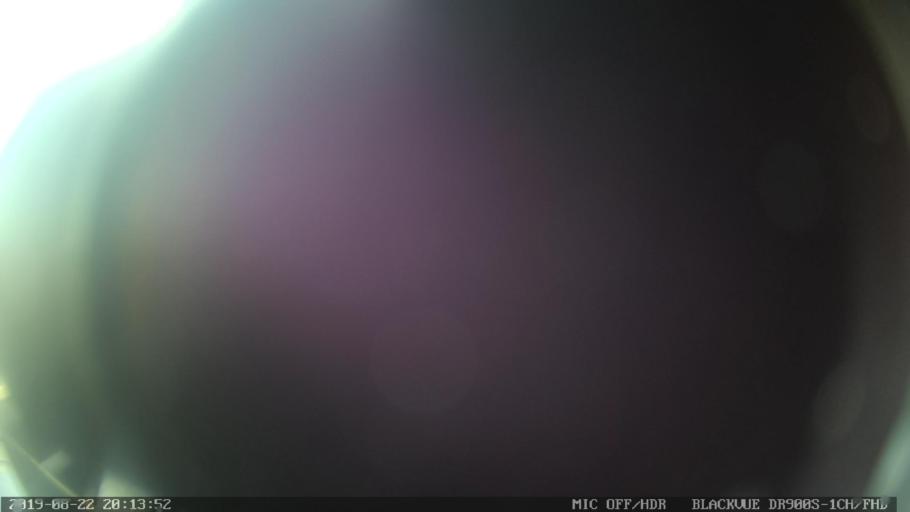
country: PT
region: Guarda
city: Alcains
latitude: 39.9240
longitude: -7.4164
